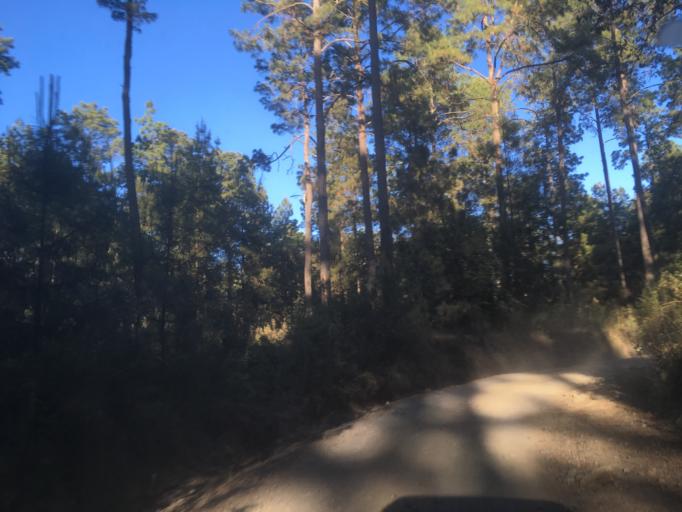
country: MX
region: Michoacan
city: Angahuan
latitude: 19.4643
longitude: -102.2154
